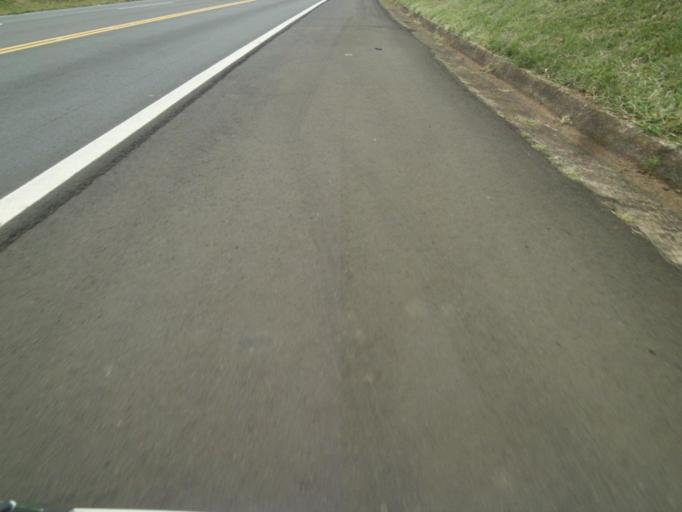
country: BR
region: Parana
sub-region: Palmeira
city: Palmeira
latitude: -25.4691
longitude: -49.7811
